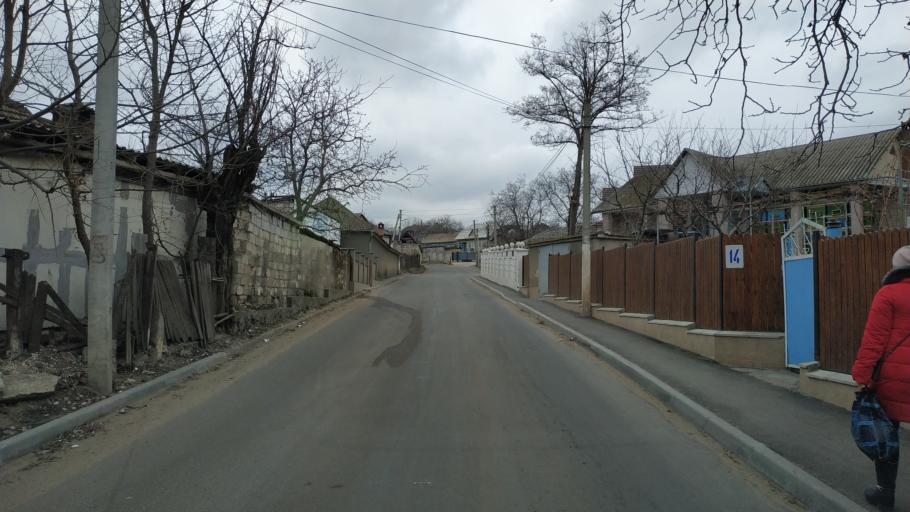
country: MD
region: Laloveni
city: Ialoveni
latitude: 46.8686
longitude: 28.7602
